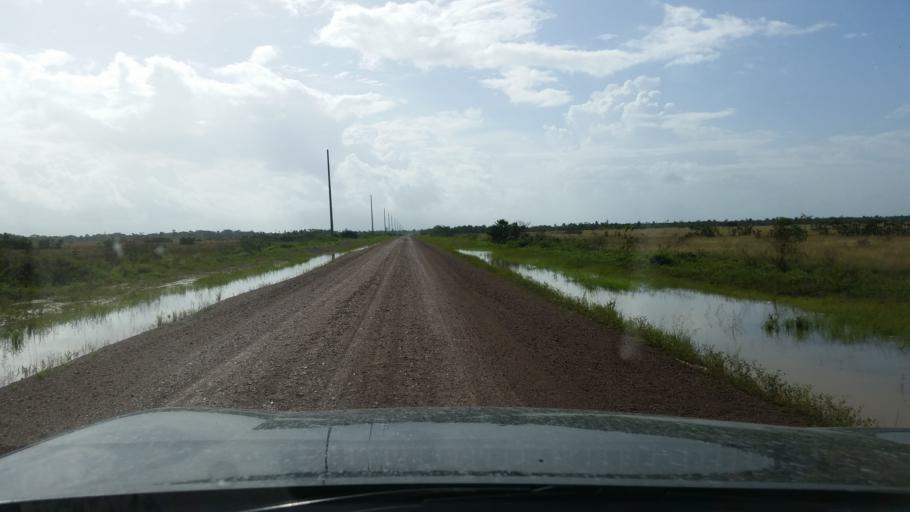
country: NI
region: Atlantico Norte (RAAN)
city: Puerto Cabezas
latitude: 14.1094
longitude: -83.5907
